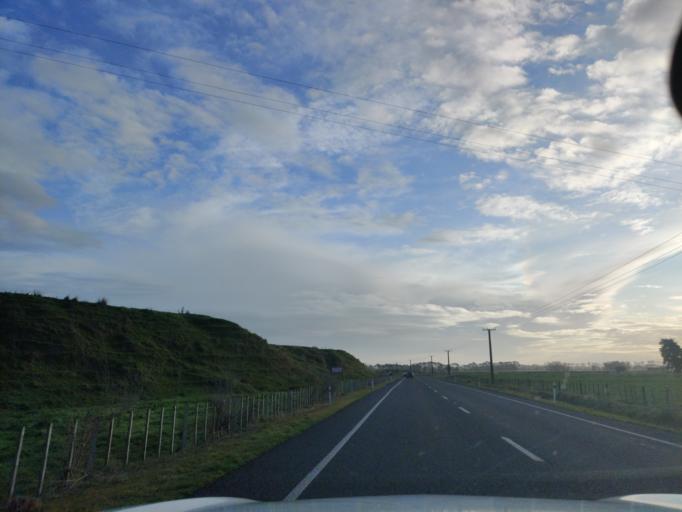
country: NZ
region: Manawatu-Wanganui
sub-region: Palmerston North City
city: Palmerston North
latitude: -40.4898
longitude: 175.4979
